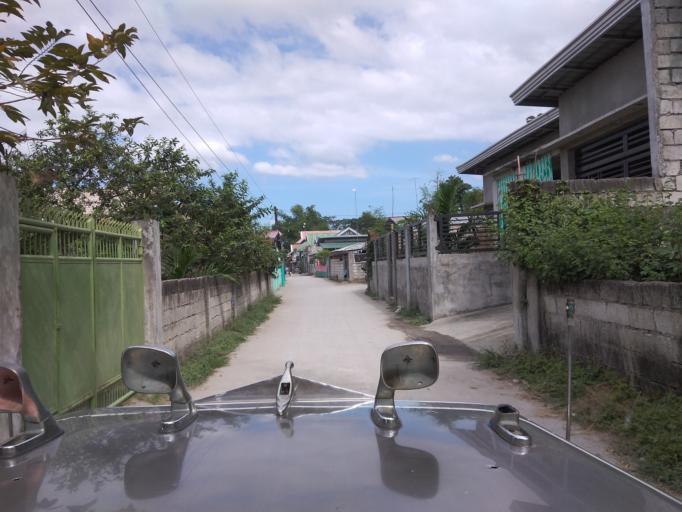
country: PH
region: Central Luzon
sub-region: Province of Pampanga
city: San Patricio
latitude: 15.1107
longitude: 120.7191
